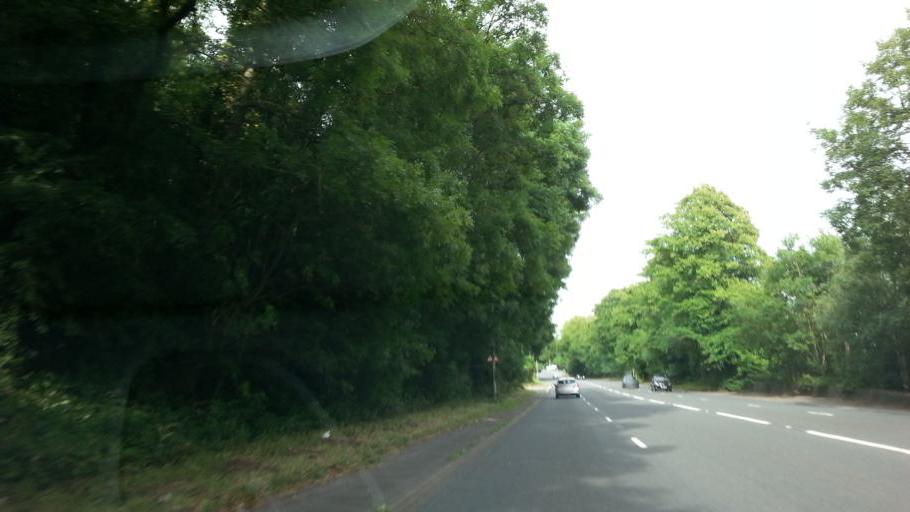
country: GB
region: Wales
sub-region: Newport
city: Marshfield
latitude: 51.5510
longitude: -3.0638
